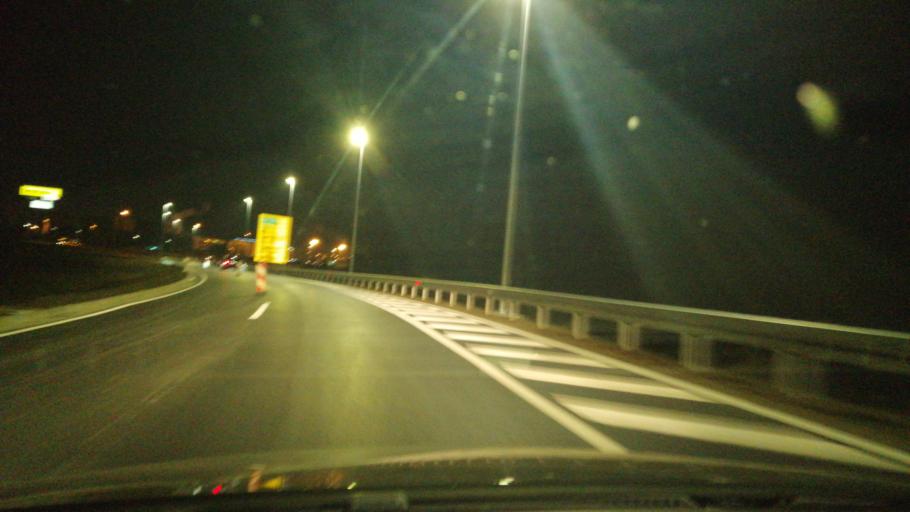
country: RS
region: Autonomna Pokrajina Vojvodina
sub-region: Juznobacki Okrug
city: Novi Sad
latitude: 45.3078
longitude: 19.8435
